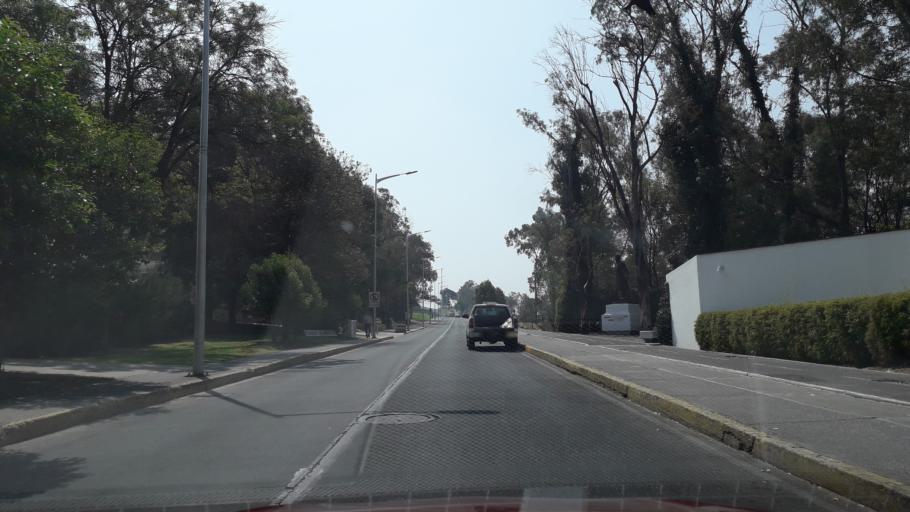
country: MX
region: Puebla
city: Puebla
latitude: 19.0565
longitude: -98.1838
